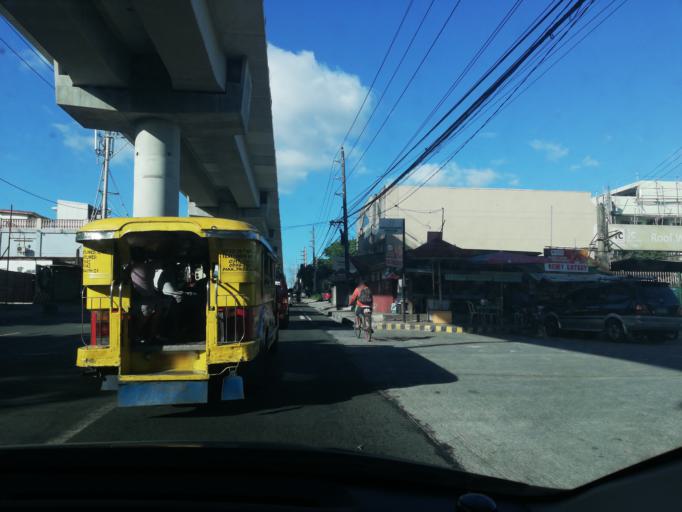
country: PH
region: Calabarzon
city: Bagong Pagasa
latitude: 14.7136
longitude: 121.0612
